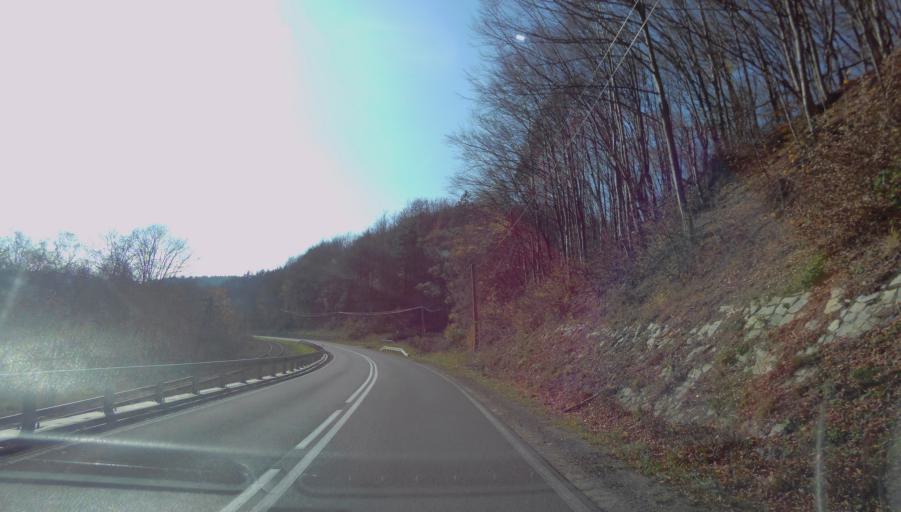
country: PL
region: Subcarpathian Voivodeship
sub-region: Powiat sanocki
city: Komancza
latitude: 49.3241
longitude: 22.0568
